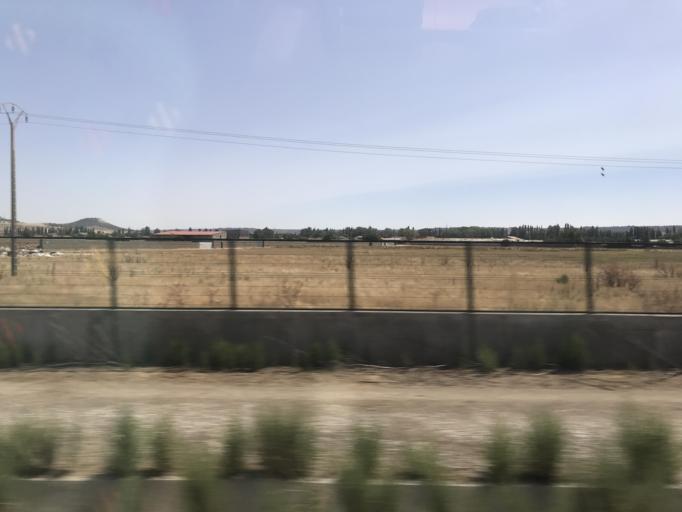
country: ES
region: Castille and Leon
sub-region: Provincia de Valladolid
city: Santovenia de Pisuerga
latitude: 41.6705
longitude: -4.6973
